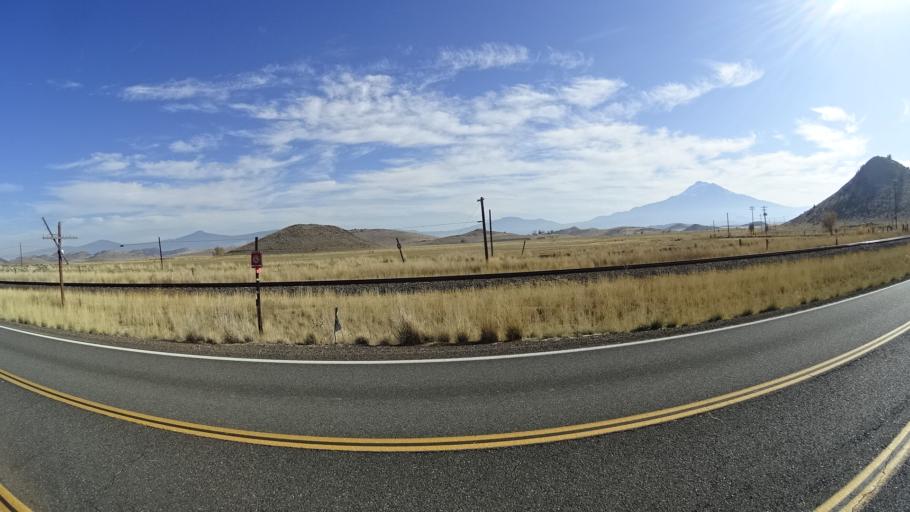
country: US
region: California
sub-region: Siskiyou County
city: Weed
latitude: 41.5389
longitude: -122.5251
